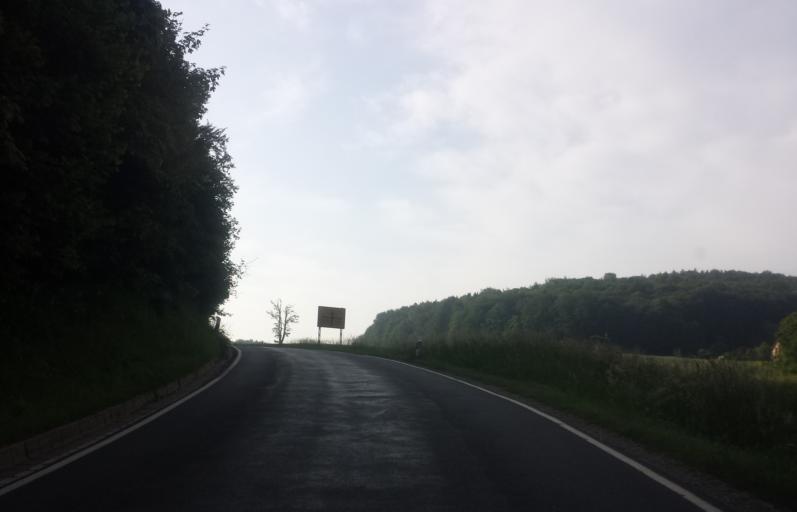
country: DE
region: Bavaria
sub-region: Upper Franconia
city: Ebermannstadt
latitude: 49.7799
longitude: 11.2241
